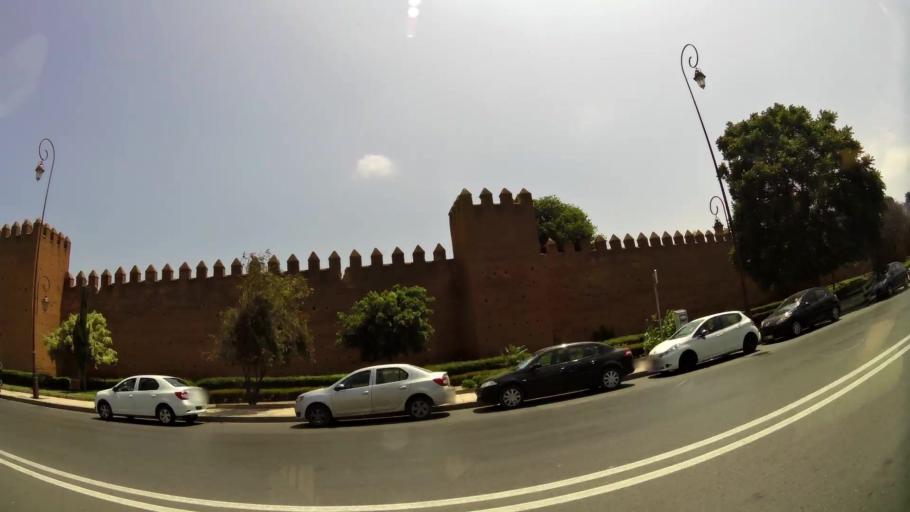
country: MA
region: Rabat-Sale-Zemmour-Zaer
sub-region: Rabat
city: Rabat
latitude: 34.0176
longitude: -6.8394
